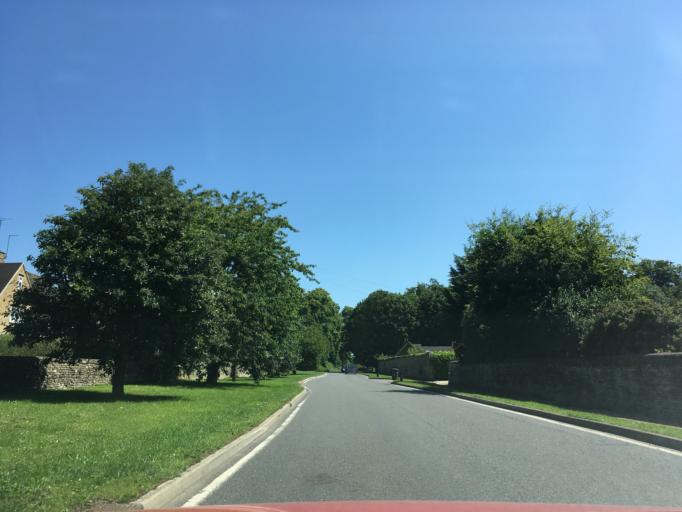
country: GB
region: England
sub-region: Oxfordshire
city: Somerton
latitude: 51.9955
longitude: -1.2490
